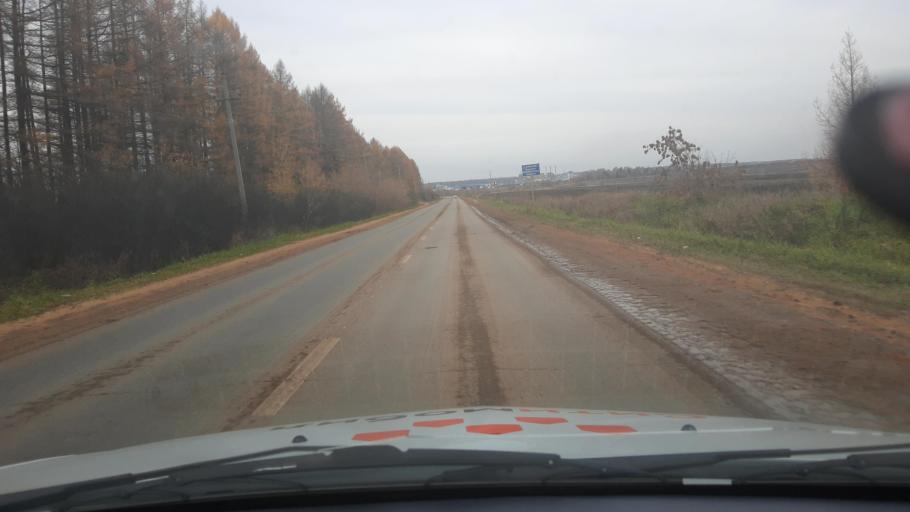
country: RU
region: Bashkortostan
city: Iglino
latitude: 54.7410
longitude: 56.2549
